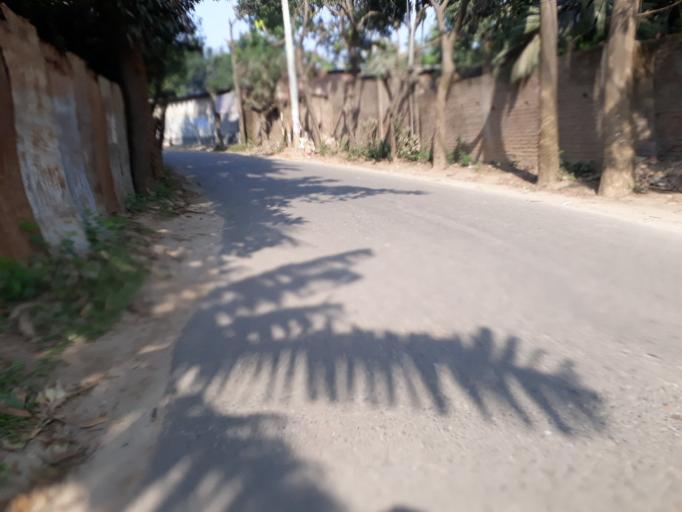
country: BD
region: Dhaka
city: Tungi
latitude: 23.8778
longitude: 90.3106
